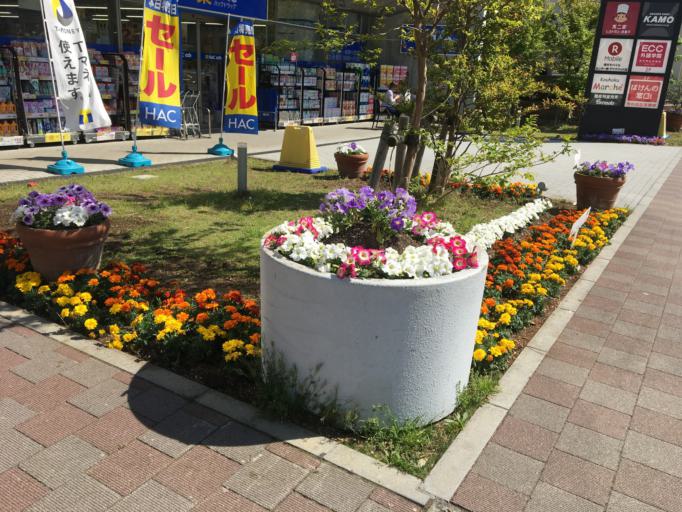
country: JP
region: Tokyo
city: Chofugaoka
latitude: 35.5440
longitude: 139.5739
